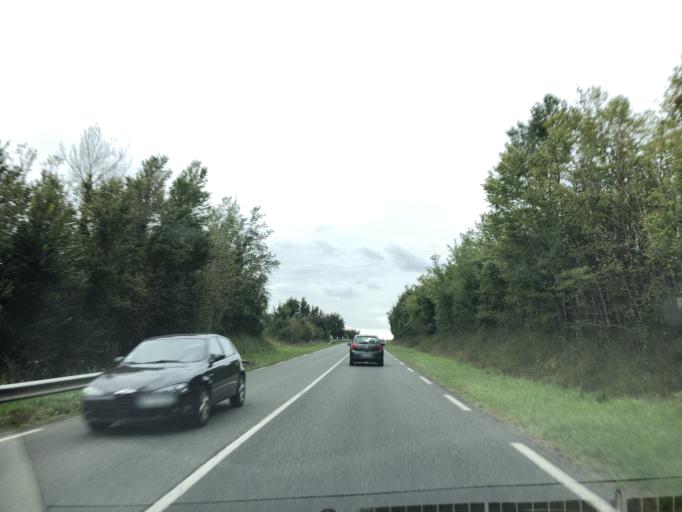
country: FR
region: Picardie
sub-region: Departement de la Somme
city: Abbeville
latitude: 50.1056
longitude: 1.7642
